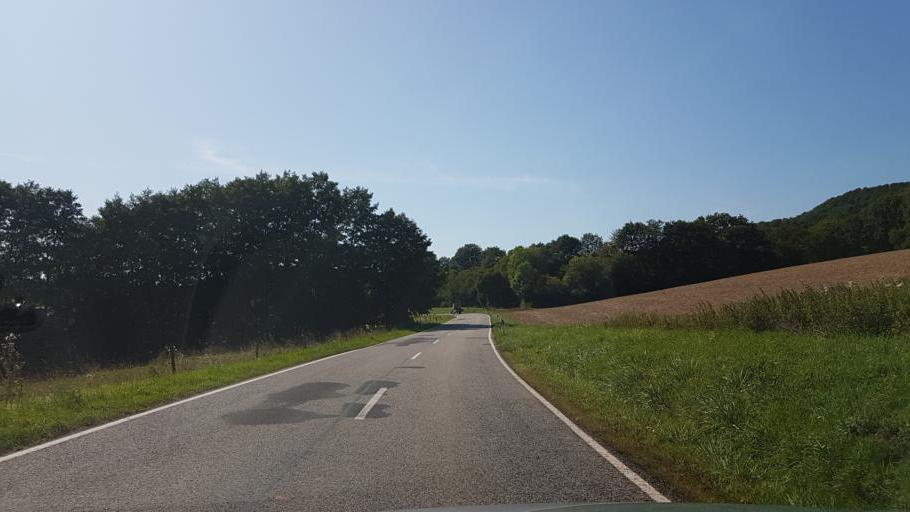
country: DE
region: Saarland
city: Tholey
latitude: 49.4962
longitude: 6.9866
